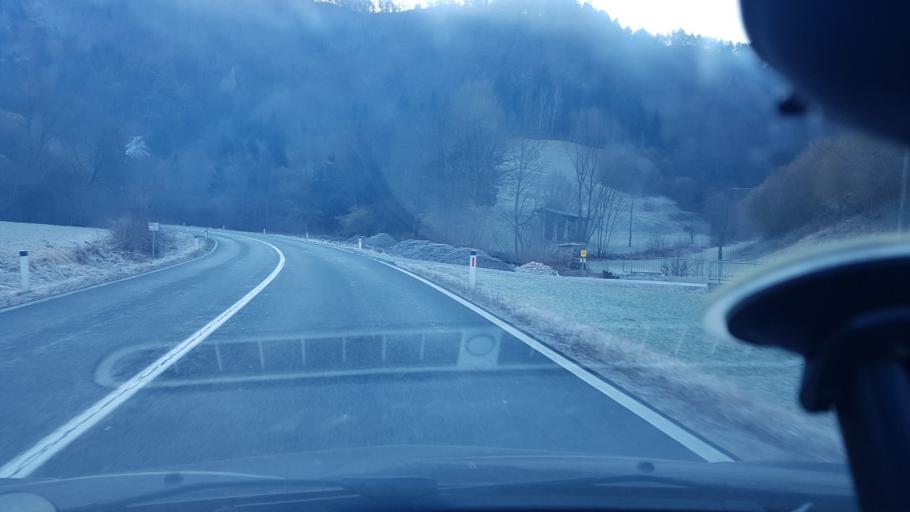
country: SI
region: Moravce
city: Moravce
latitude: 46.1749
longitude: 14.8281
